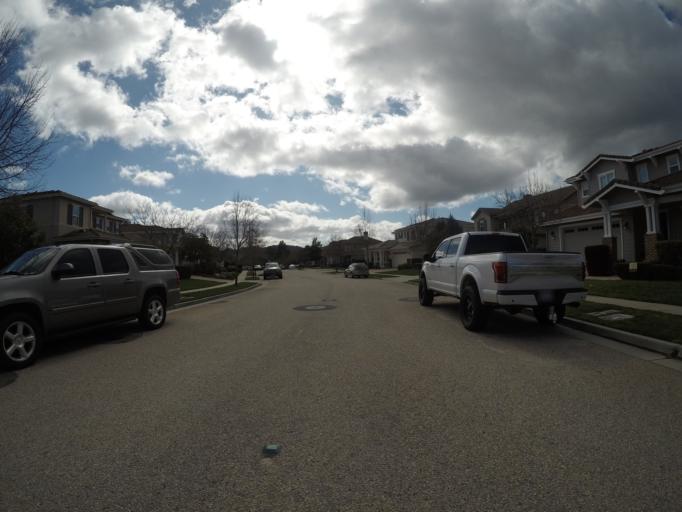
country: US
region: California
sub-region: Santa Cruz County
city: Scotts Valley
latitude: 37.0709
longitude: -122.0038
